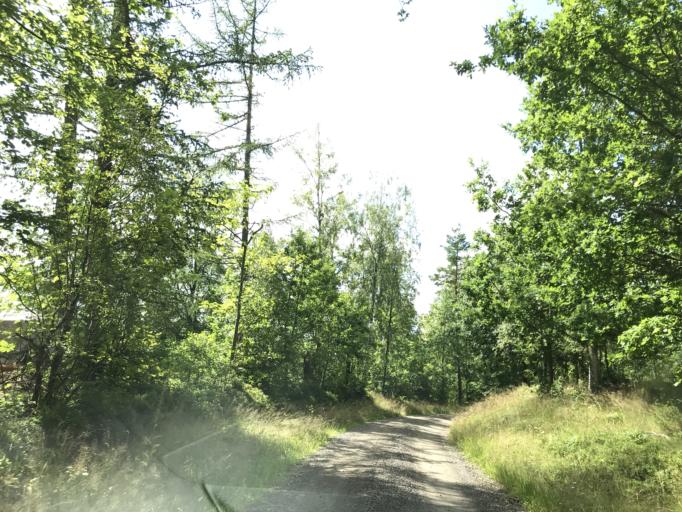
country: SE
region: Halland
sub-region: Laholms Kommun
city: Knared
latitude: 56.5082
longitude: 13.2912
